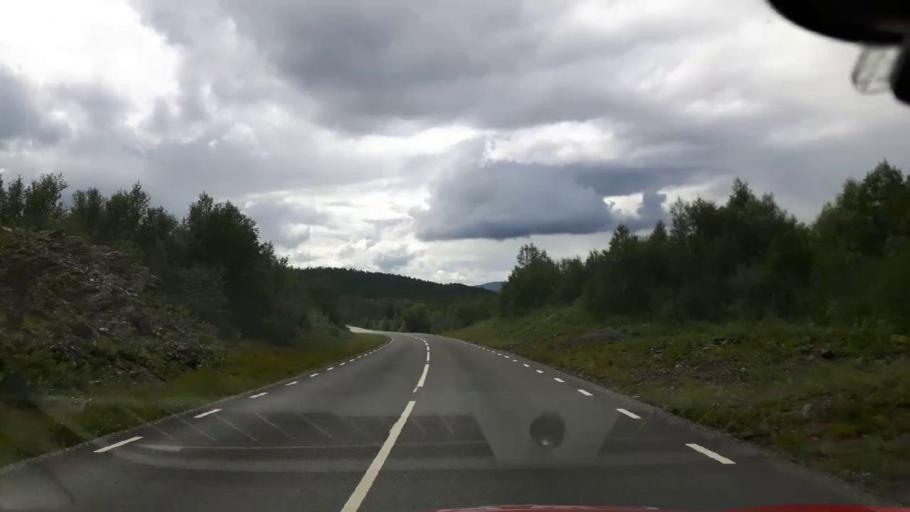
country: NO
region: Nordland
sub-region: Hattfjelldal
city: Hattfjelldal
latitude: 64.9844
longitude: 14.2130
